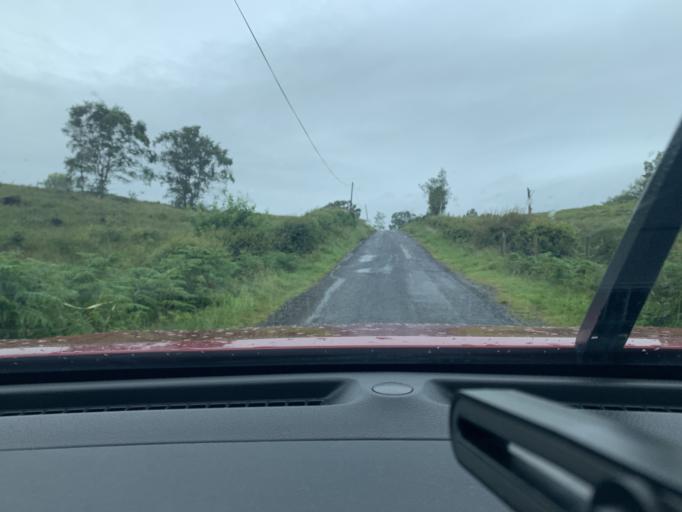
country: GB
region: Northern Ireland
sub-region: Fermanagh District
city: Enniskillen
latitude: 54.2509
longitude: -7.8176
